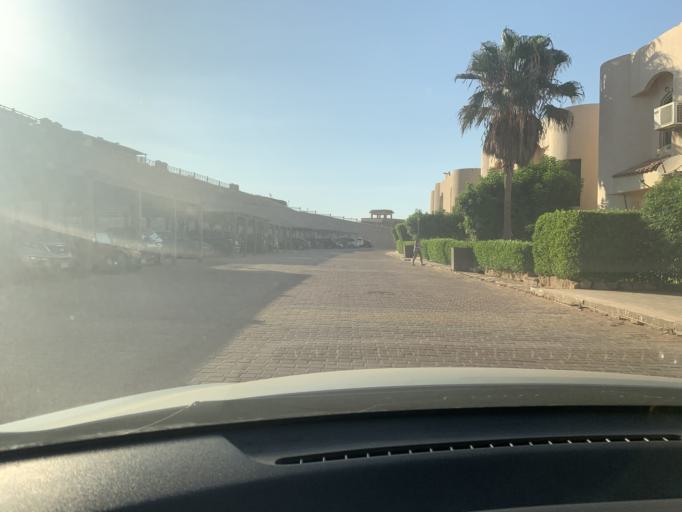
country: EG
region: As Suways
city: Ain Sukhna
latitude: 29.3747
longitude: 32.5709
